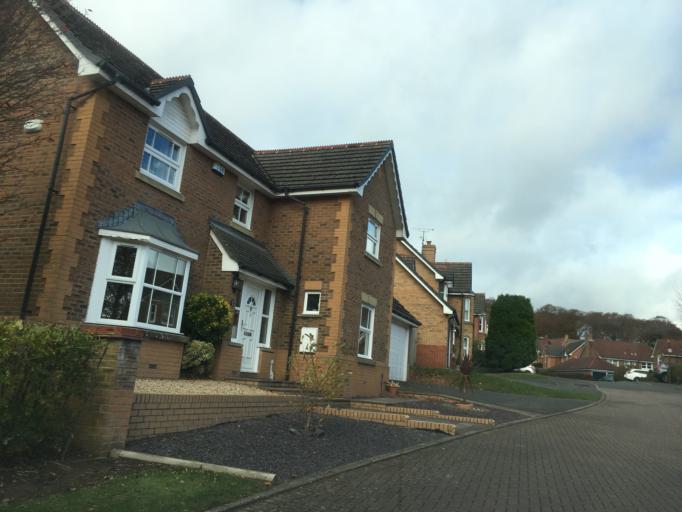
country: GB
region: Scotland
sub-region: Midlothian
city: Loanhead
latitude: 55.8994
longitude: -3.1915
